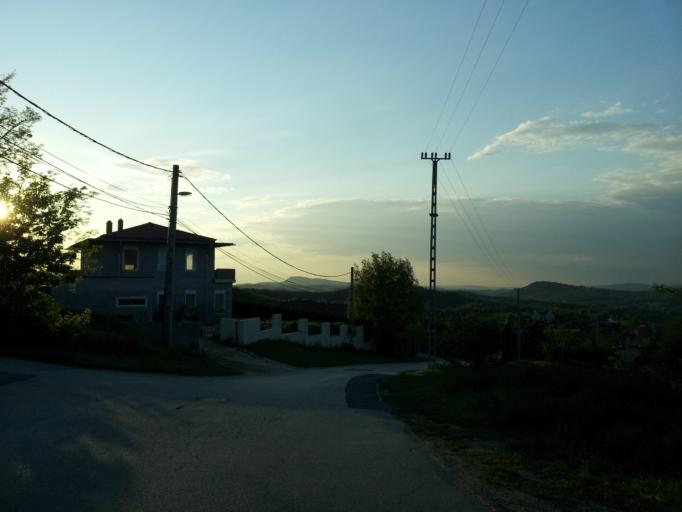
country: HU
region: Pest
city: Piliscsaba
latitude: 47.6255
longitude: 18.8120
